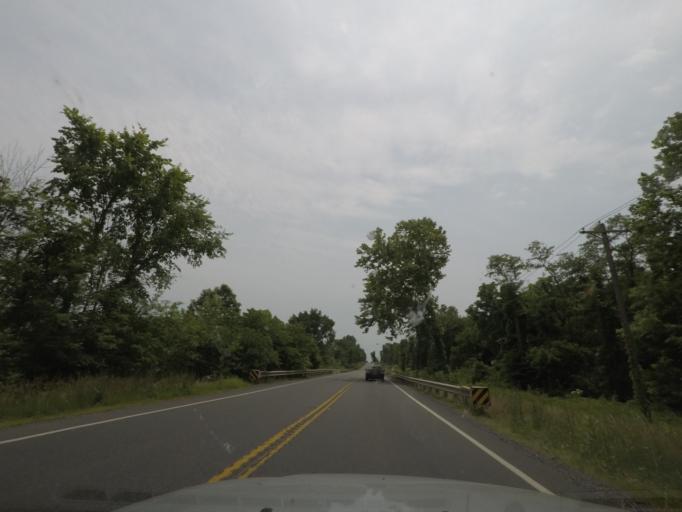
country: US
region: Virginia
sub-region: Prince William County
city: Bull Run Mountain Estates
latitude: 38.9134
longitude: -77.6282
